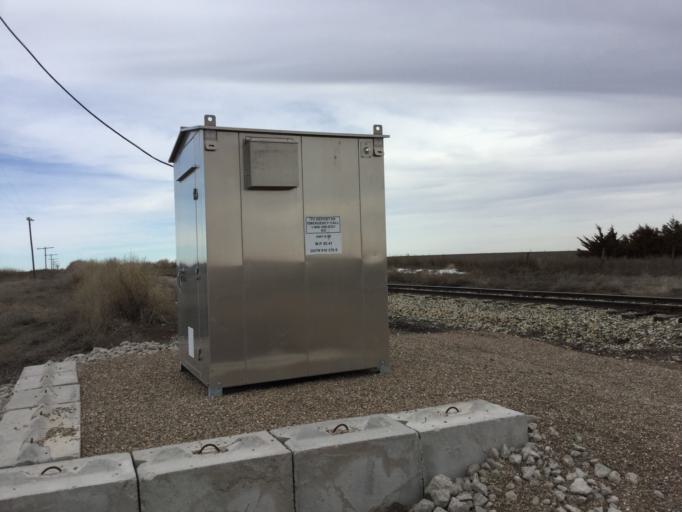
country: US
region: Kansas
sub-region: Lane County
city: Dighton
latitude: 38.4817
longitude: -100.4059
